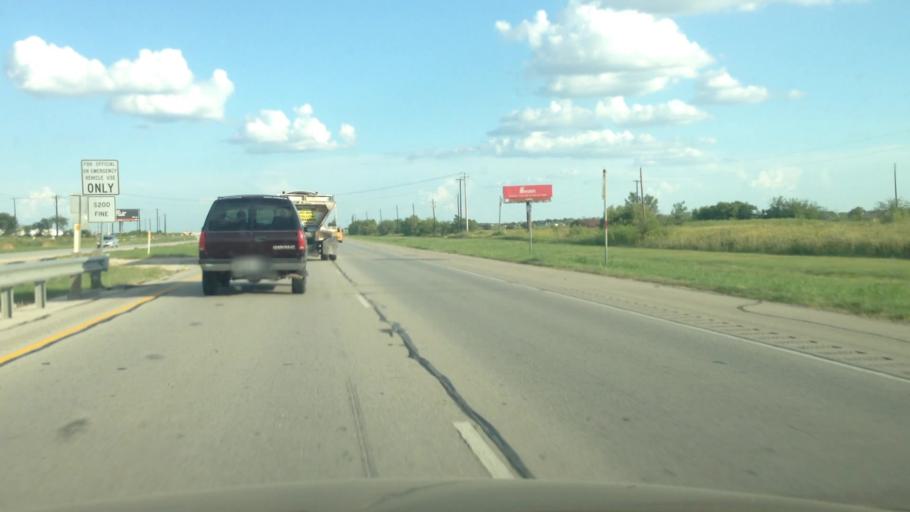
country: US
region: Texas
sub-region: Tarrant County
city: Blue Mound
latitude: 32.9057
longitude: -97.3394
